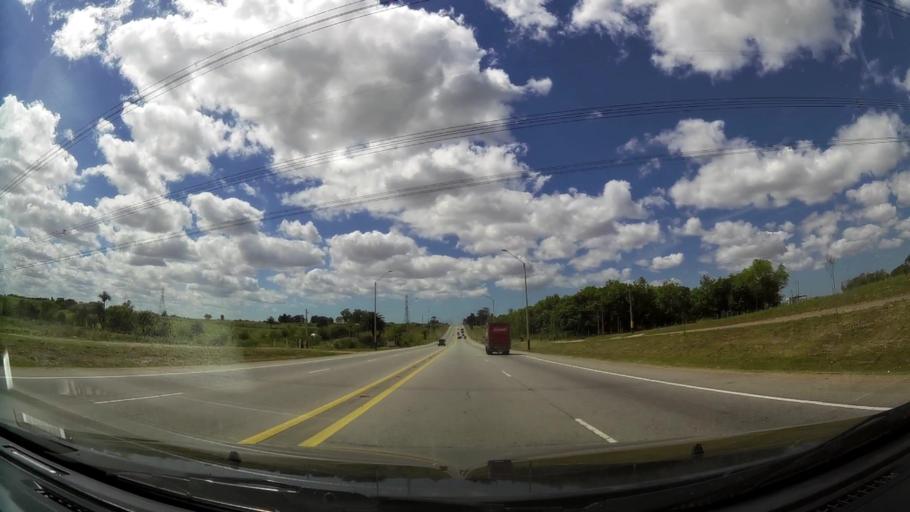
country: UY
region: Canelones
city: Colonia Nicolich
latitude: -34.7966
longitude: -56.0648
